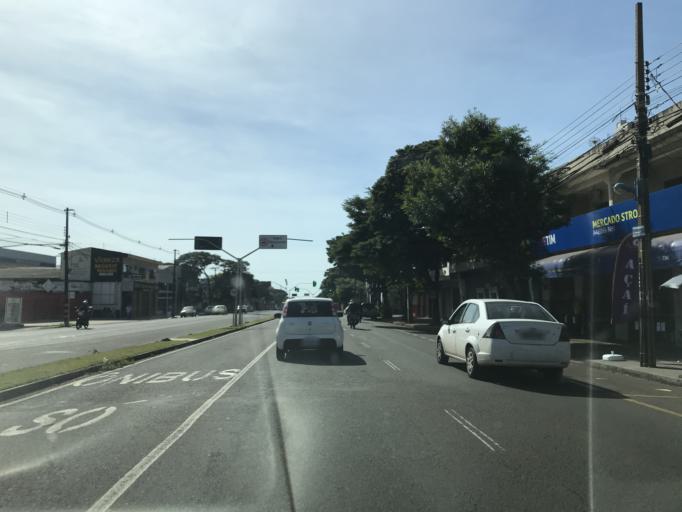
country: BR
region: Parana
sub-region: Maringa
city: Maringa
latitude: -23.4092
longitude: -51.9310
